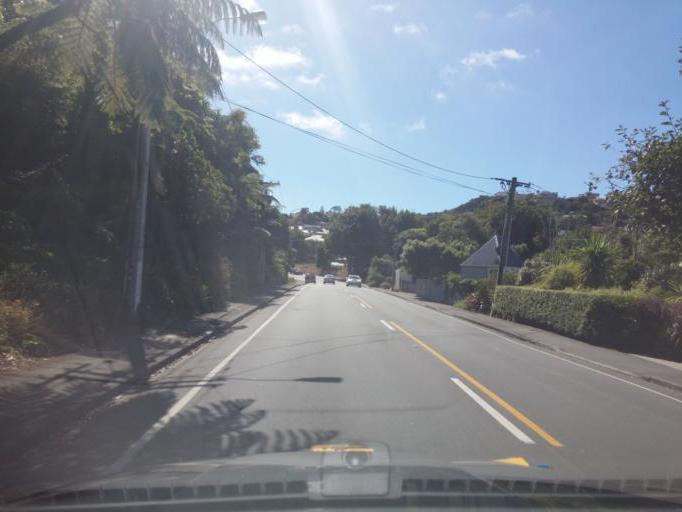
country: NZ
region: Wellington
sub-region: Wellington City
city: Wellington
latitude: -41.2413
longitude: 174.7931
